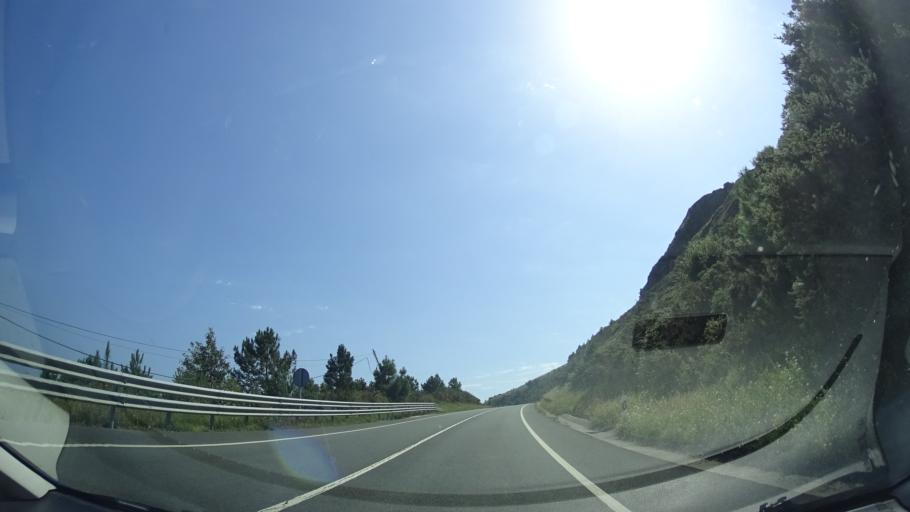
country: ES
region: Basque Country
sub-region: Bizkaia
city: Bakio
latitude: 43.4406
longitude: -2.7730
